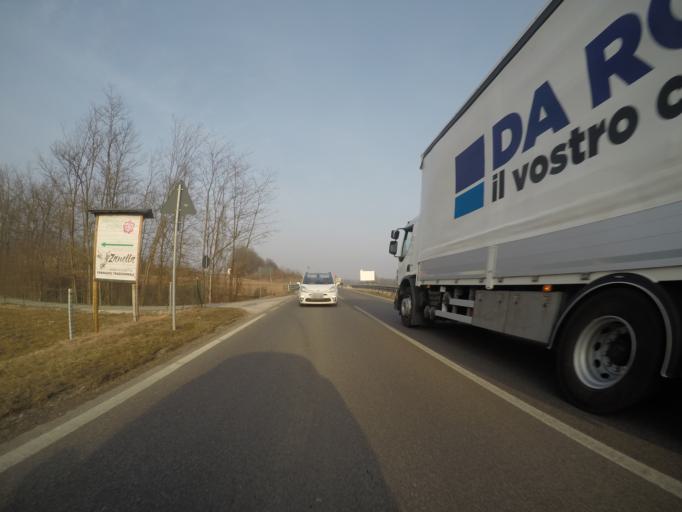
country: IT
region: Veneto
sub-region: Provincia di Belluno
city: Lentiai
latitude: 46.0611
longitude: 12.0066
